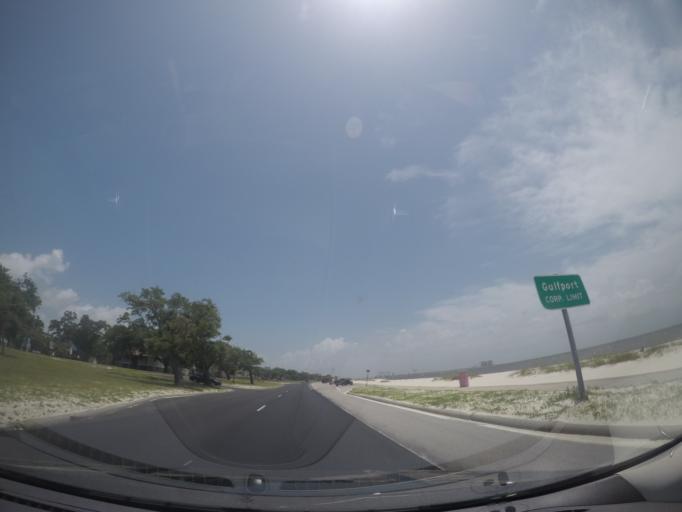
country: US
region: Mississippi
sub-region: Harrison County
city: Long Beach
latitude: 30.3546
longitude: -89.1251
